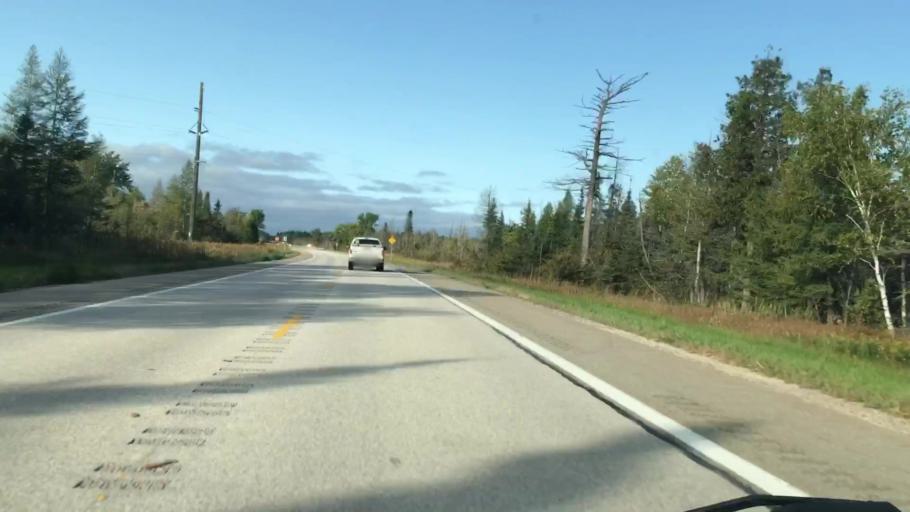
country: US
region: Michigan
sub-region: Luce County
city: Newberry
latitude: 46.3191
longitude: -85.1907
